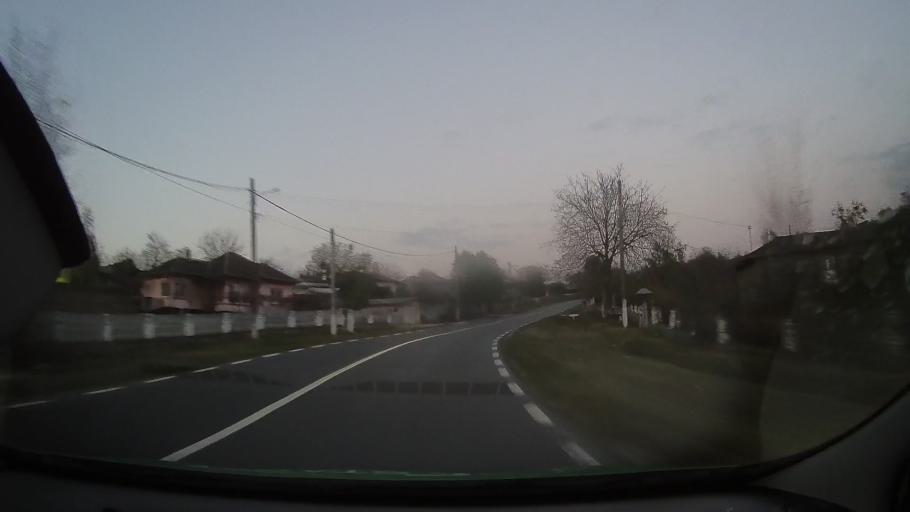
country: RO
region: Constanta
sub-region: Comuna Baneasa
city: Baneasa
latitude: 44.0642
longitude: 27.7049
